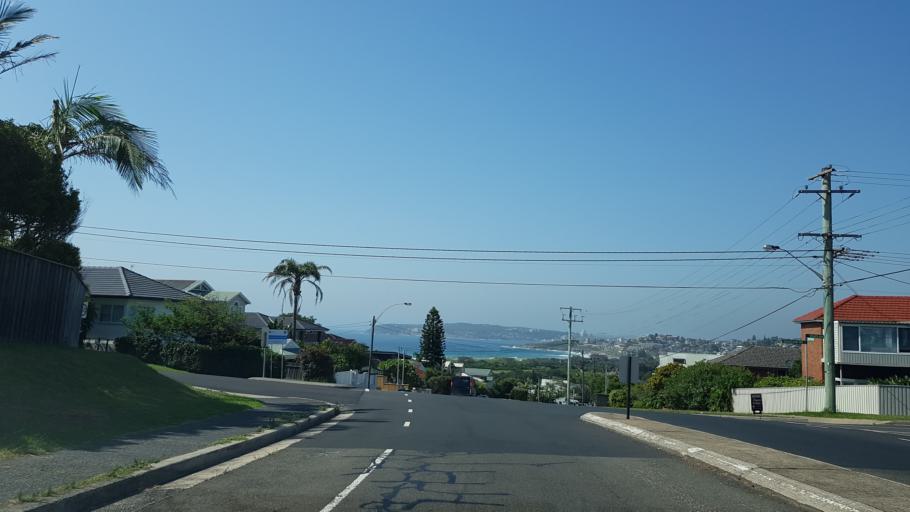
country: AU
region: New South Wales
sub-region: Warringah
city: North Curl Curl
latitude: -33.7603
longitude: 151.2958
